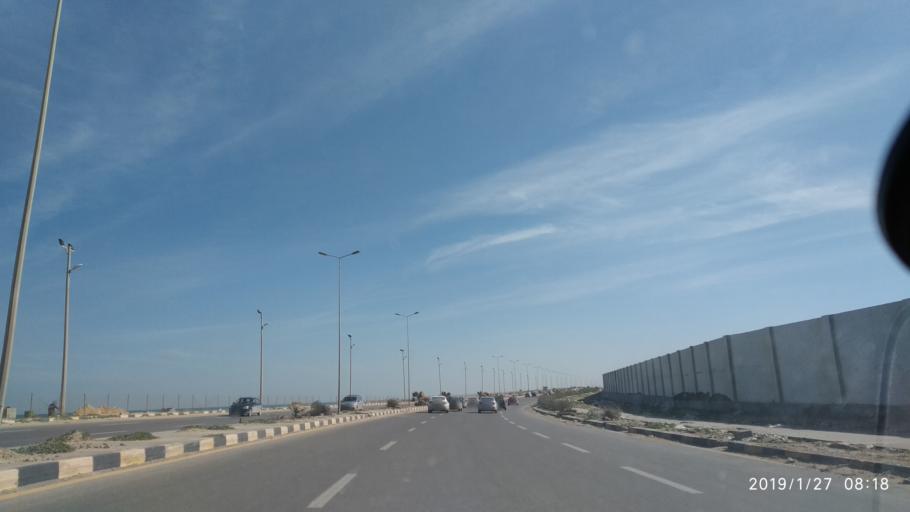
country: LY
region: Tripoli
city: Tagiura
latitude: 32.9086
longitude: 13.2887
